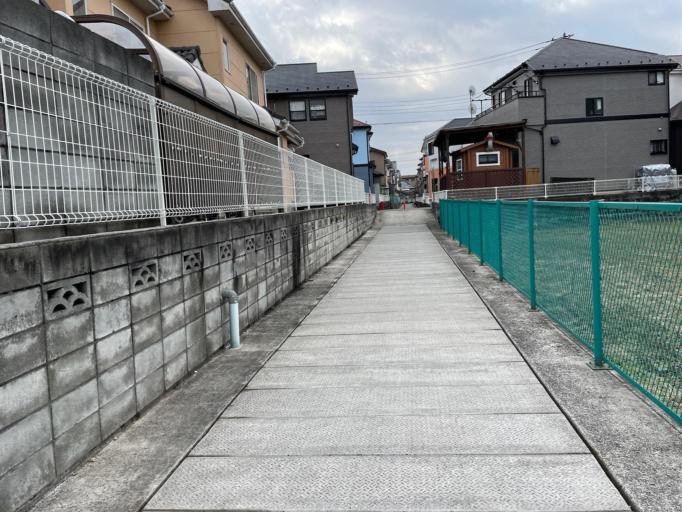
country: JP
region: Saitama
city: Yashio-shi
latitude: 35.8525
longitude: 139.8438
